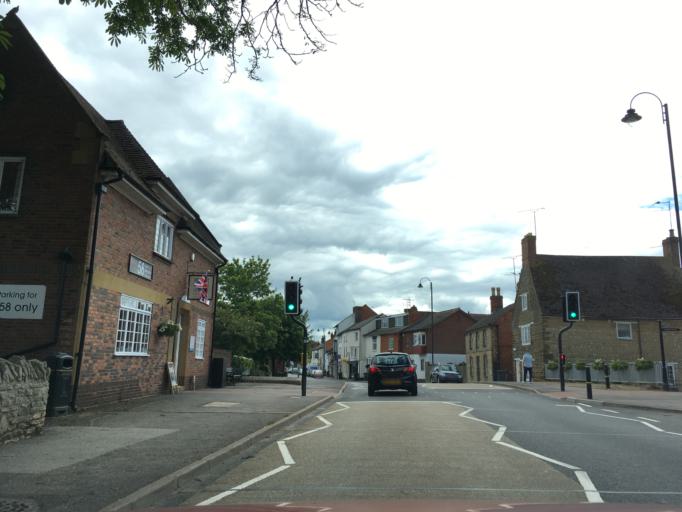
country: GB
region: England
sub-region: Northamptonshire
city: Towcester
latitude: 52.1307
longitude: -0.9873
